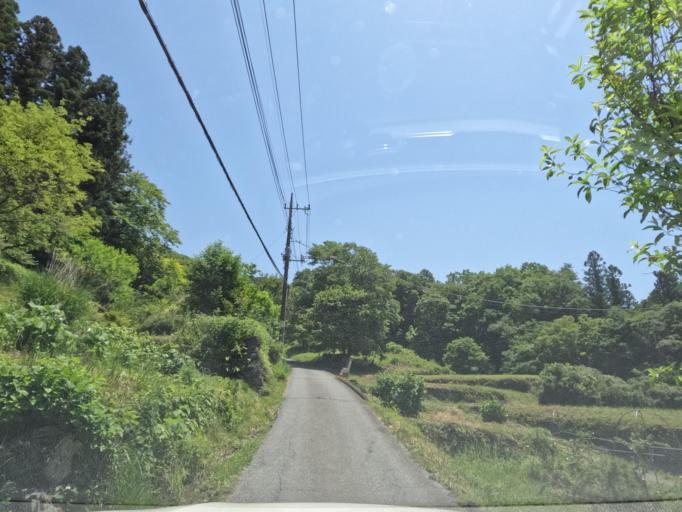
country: JP
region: Saitama
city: Chichibu
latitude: 36.0493
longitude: 139.1059
